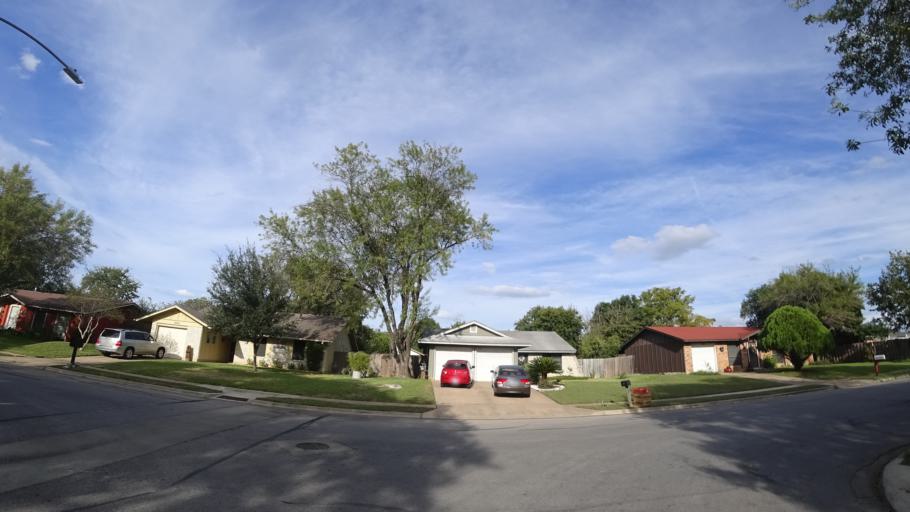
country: US
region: Texas
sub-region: Travis County
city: Onion Creek
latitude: 30.1935
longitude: -97.7579
